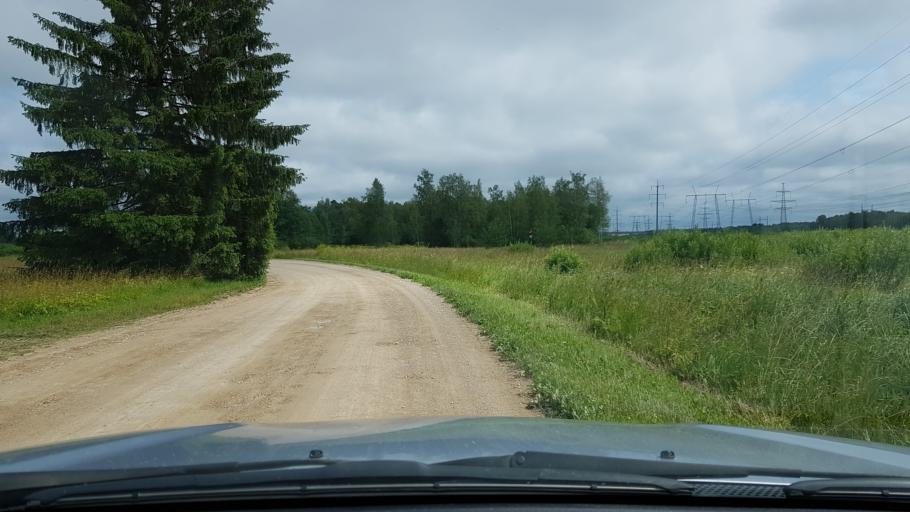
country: EE
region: Ida-Virumaa
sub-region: Narva-Joesuu linn
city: Narva-Joesuu
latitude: 59.3662
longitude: 28.0713
